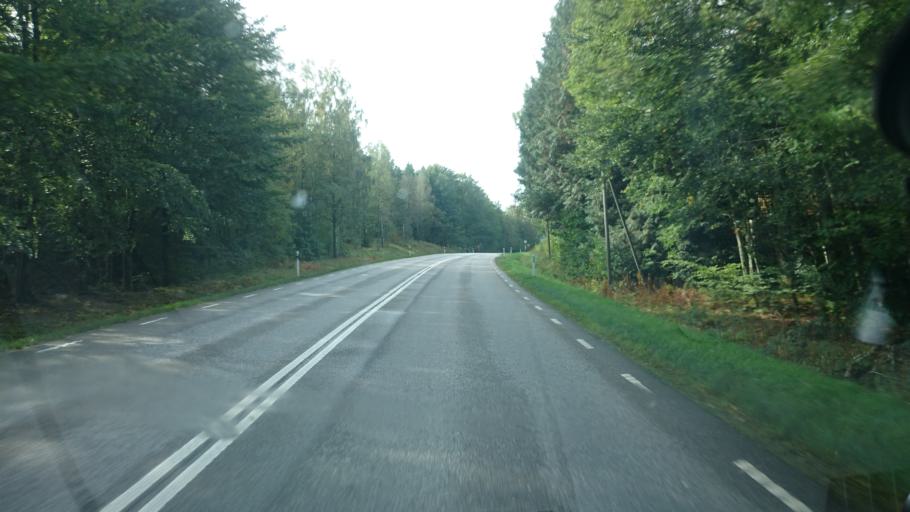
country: SE
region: Vaestra Goetaland
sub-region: Alingsas Kommun
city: Sollebrunn
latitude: 58.0673
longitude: 12.4791
